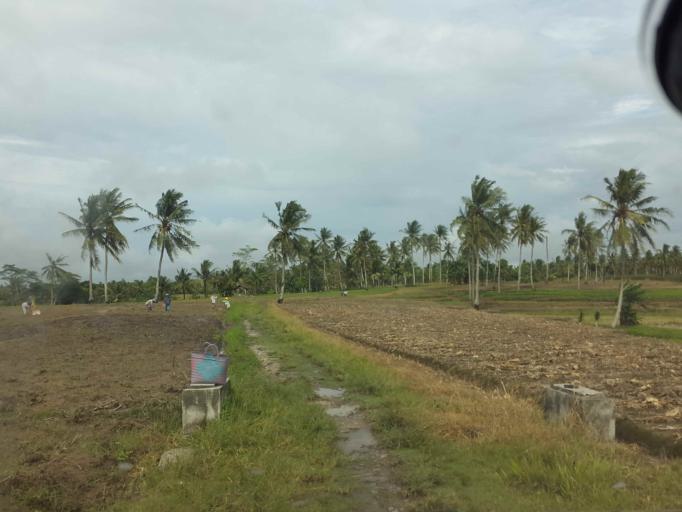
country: ID
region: Lampung
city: Palas
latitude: -5.6251
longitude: 105.6432
